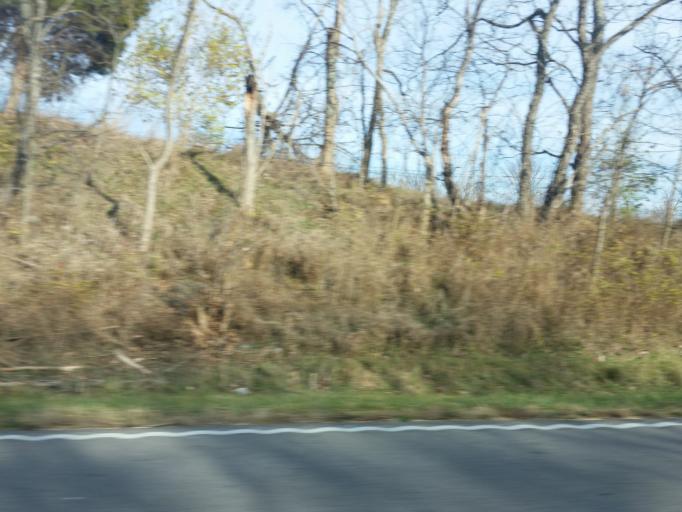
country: US
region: Kentucky
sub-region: Pendleton County
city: Falmouth
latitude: 38.7173
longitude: -84.3719
